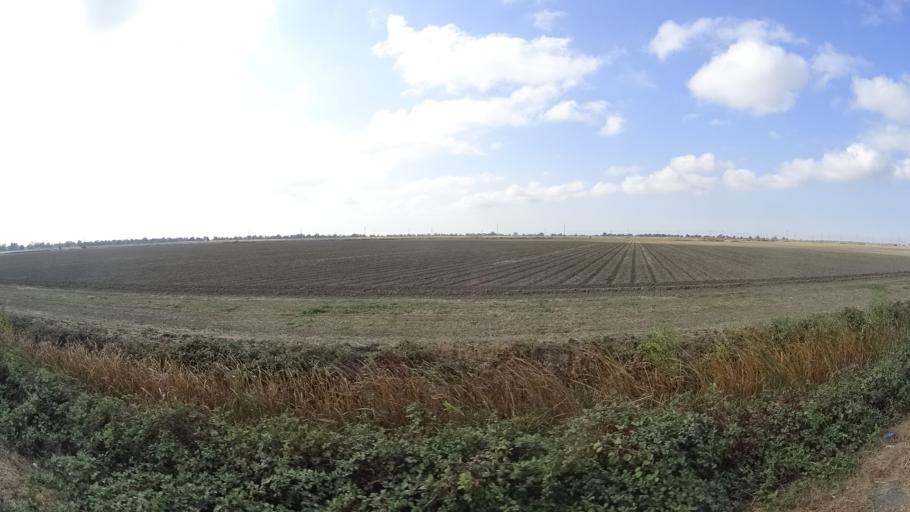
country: US
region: California
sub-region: Yolo County
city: Woodland
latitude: 38.8080
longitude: -121.7303
